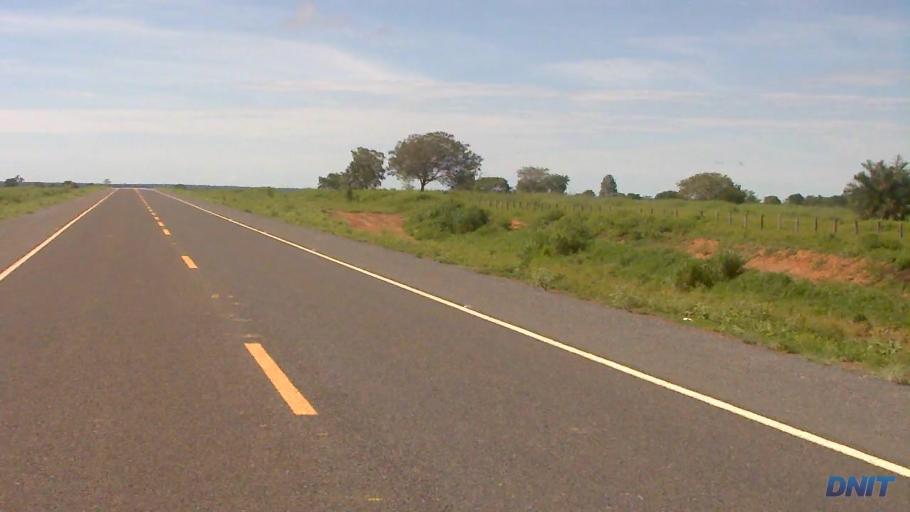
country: BR
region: Goias
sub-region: Sao Miguel Do Araguaia
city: Sao Miguel do Araguaia
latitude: -13.4798
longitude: -50.1122
